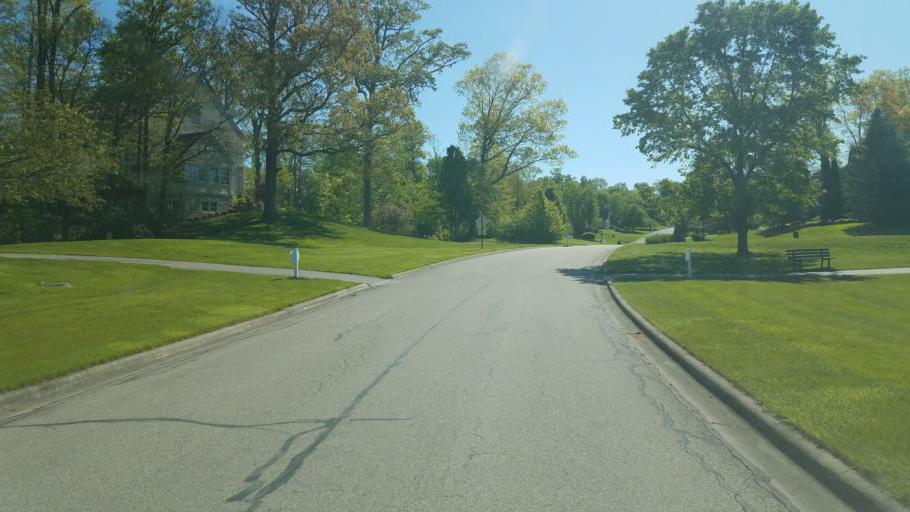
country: US
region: Ohio
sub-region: Franklin County
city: Westerville
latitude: 40.1713
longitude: -82.9467
